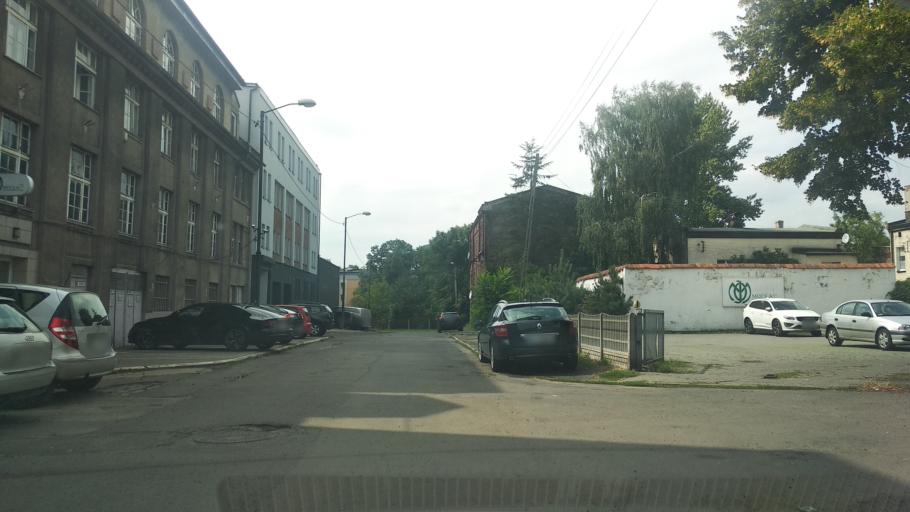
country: PL
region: Silesian Voivodeship
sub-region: Chorzow
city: Chorzow
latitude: 50.2666
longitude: 18.9859
